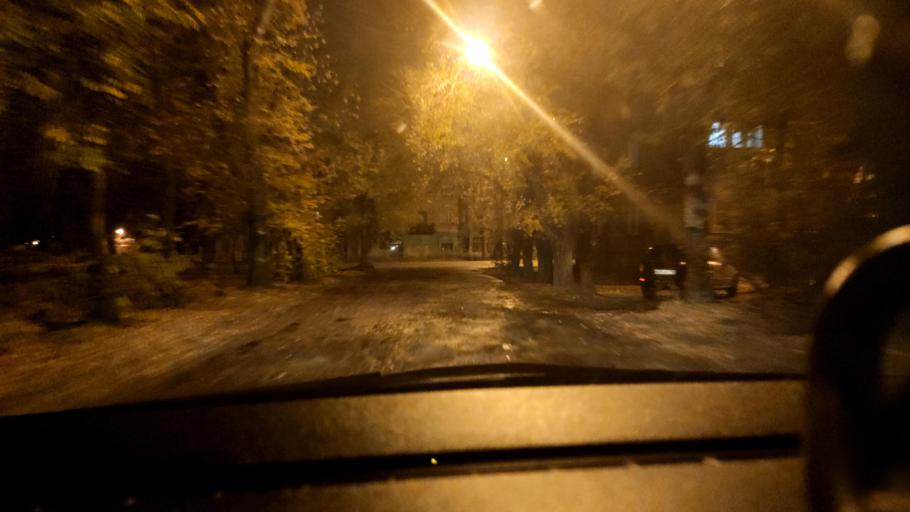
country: RU
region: Voronezj
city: Voronezh
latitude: 51.6755
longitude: 39.1463
